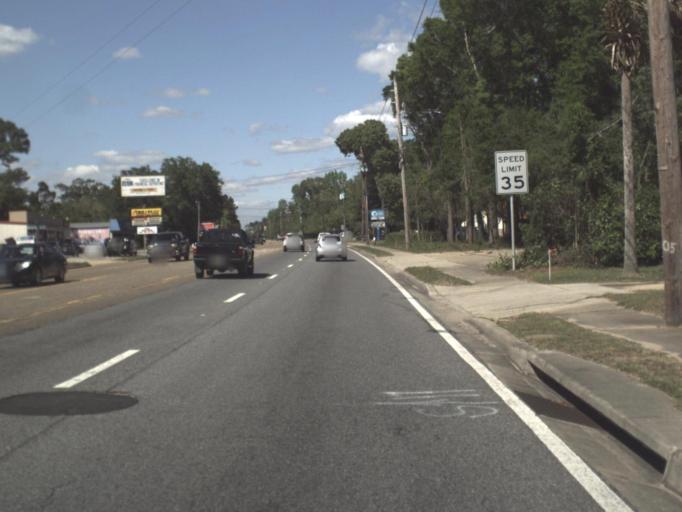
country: US
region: Florida
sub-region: Escambia County
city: Ferry Pass
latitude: 30.5178
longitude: -87.2148
